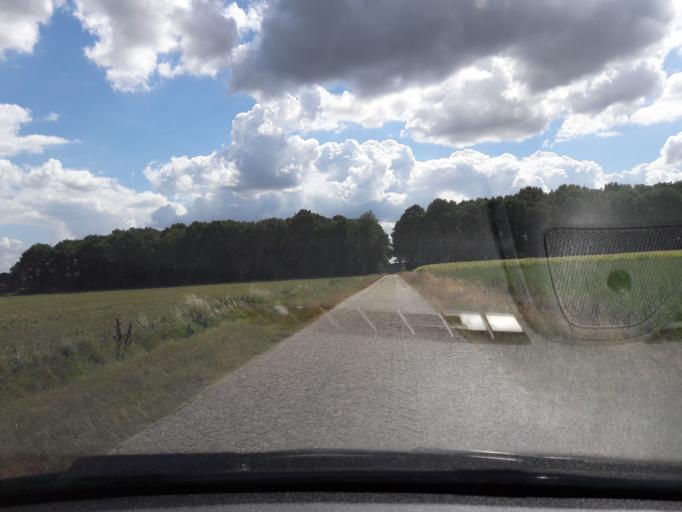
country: NL
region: Drenthe
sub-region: Gemeente Borger-Odoorn
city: Borger
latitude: 52.9385
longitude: 6.7964
